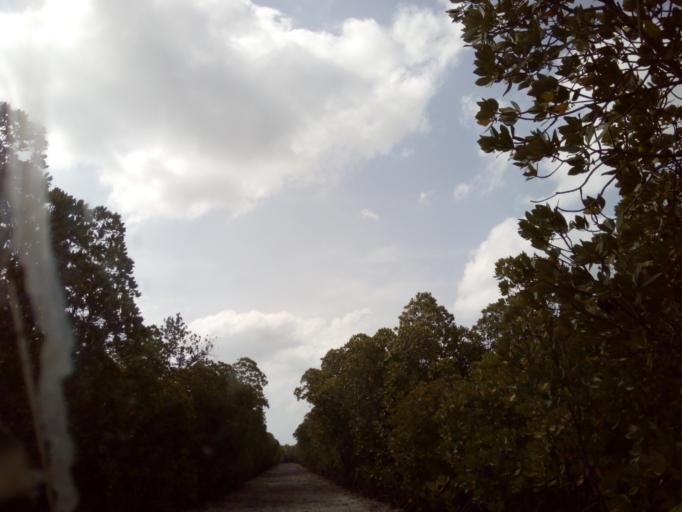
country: TZ
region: Zanzibar Central/South
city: Mahonda
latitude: -6.3198
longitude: 39.3884
